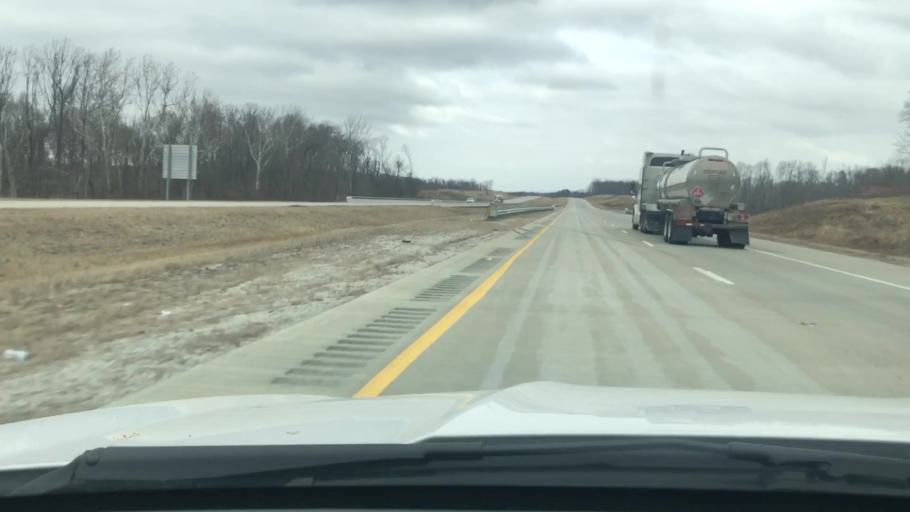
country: US
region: Indiana
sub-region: Carroll County
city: Delphi
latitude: 40.5786
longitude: -86.6479
